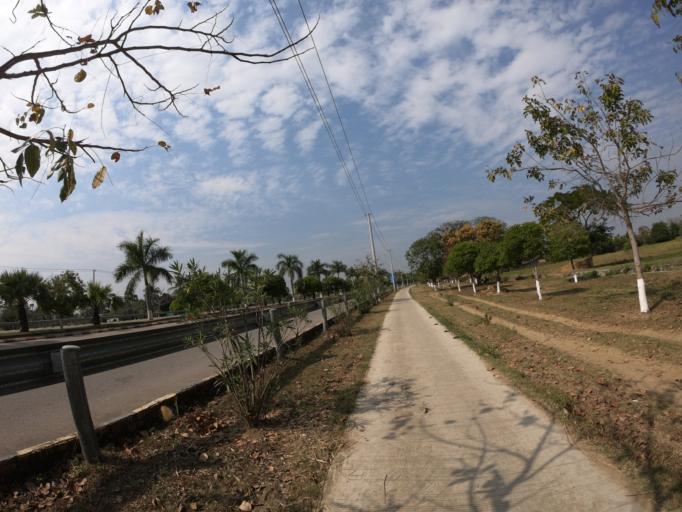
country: MM
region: Mandalay
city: Pyinmana
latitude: 19.6247
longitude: 96.1677
